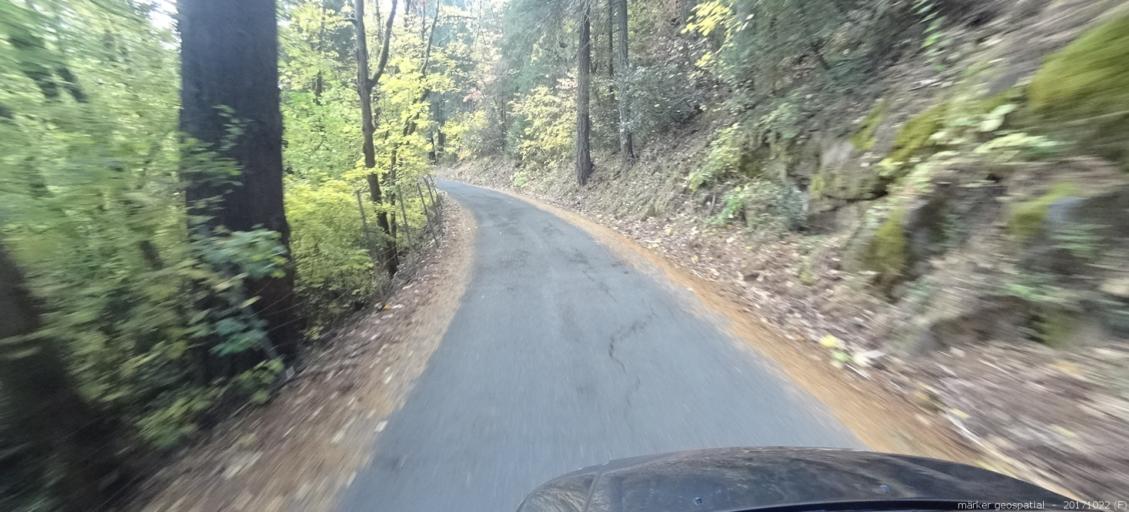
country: US
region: California
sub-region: Siskiyou County
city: Dunsmuir
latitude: 41.1612
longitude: -122.2891
